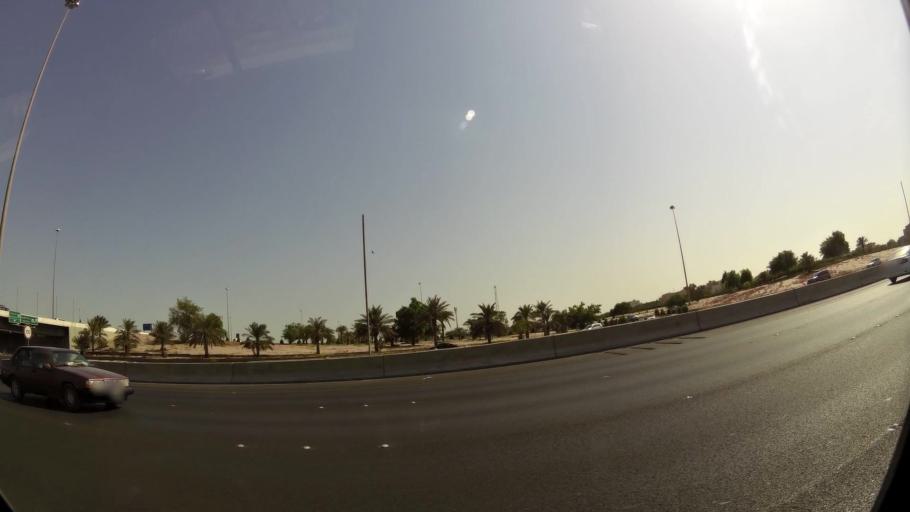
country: KW
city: Bayan
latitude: 29.3137
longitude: 48.0517
